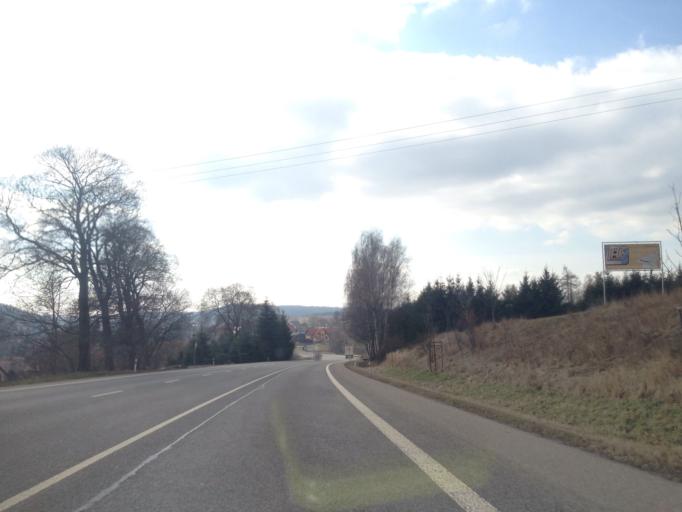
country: CZ
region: Kralovehradecky
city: Nova Paka
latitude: 50.5068
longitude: 15.5387
